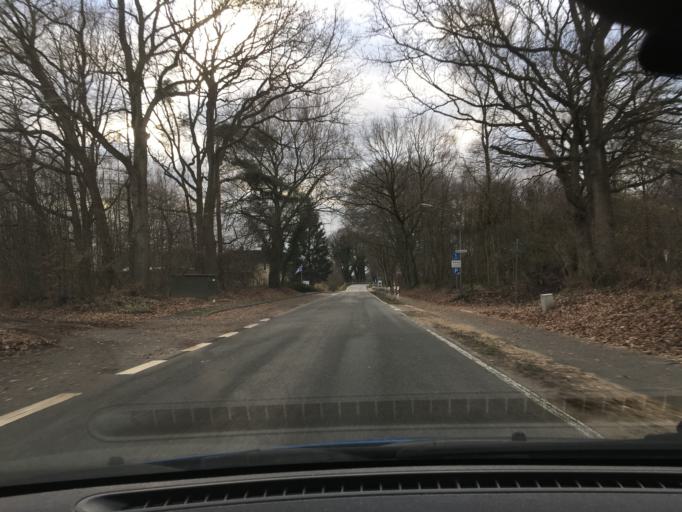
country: DE
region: Schleswig-Holstein
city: Schenefeld
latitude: 54.0483
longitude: 9.4683
